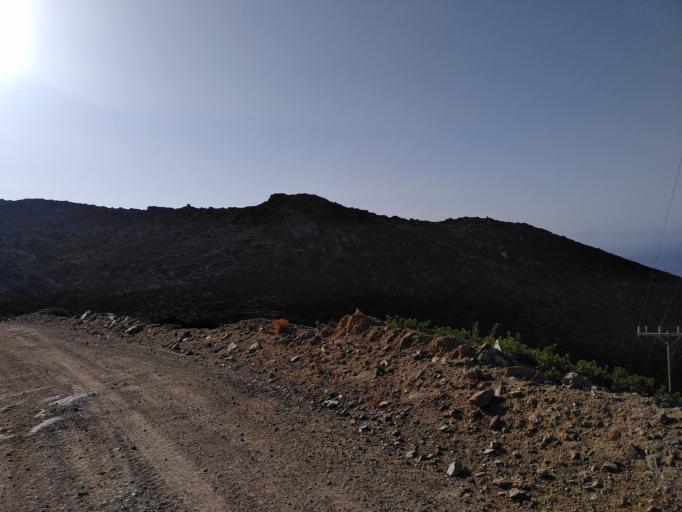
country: GR
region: South Aegean
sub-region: Nomos Kykladon
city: Ios
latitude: 36.7017
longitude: 25.3163
